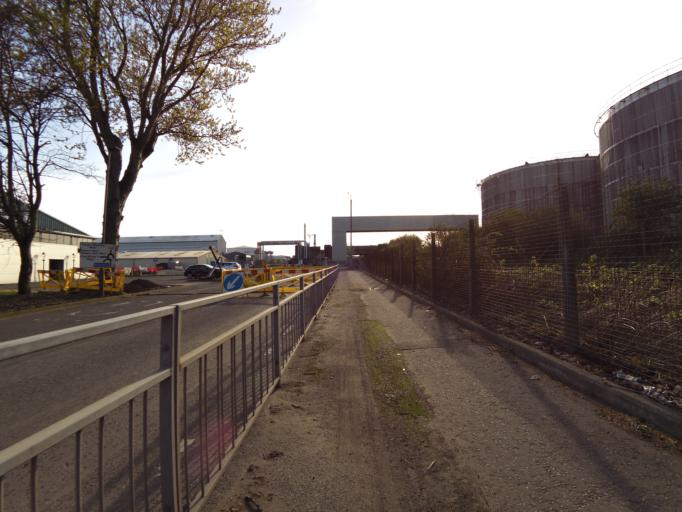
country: GB
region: Scotland
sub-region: Fife
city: Newport-On-Tay
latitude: 56.4667
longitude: -2.9414
